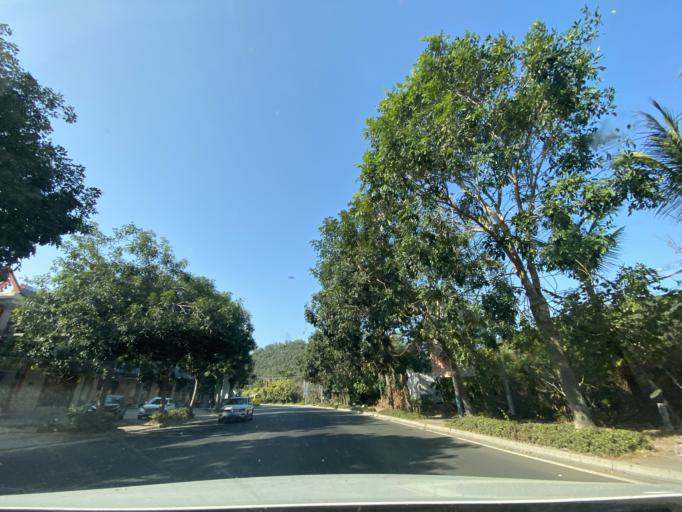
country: CN
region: Hainan
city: Yingzhou
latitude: 18.4402
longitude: 109.8495
